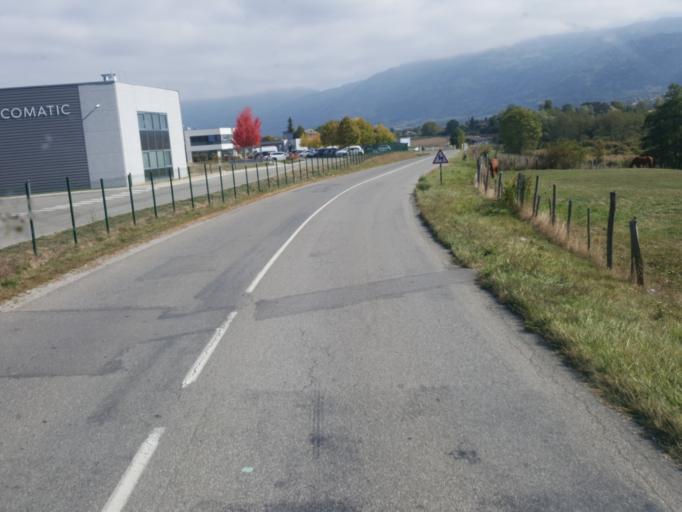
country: FR
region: Rhone-Alpes
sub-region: Departement de la Haute-Savoie
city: Ballaison
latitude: 46.2737
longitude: 6.3456
